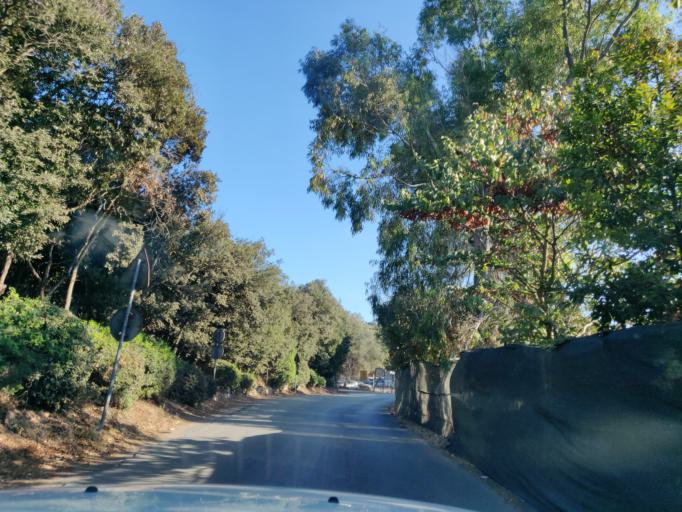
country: IT
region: Tuscany
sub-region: Provincia di Grosseto
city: Orbetello Scalo
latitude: 42.4196
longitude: 11.2821
